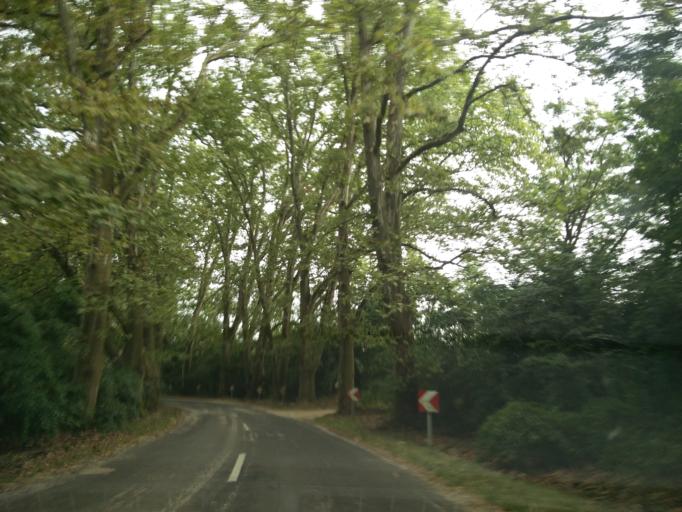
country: HU
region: Fejer
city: Bicske
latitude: 47.4377
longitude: 18.6124
